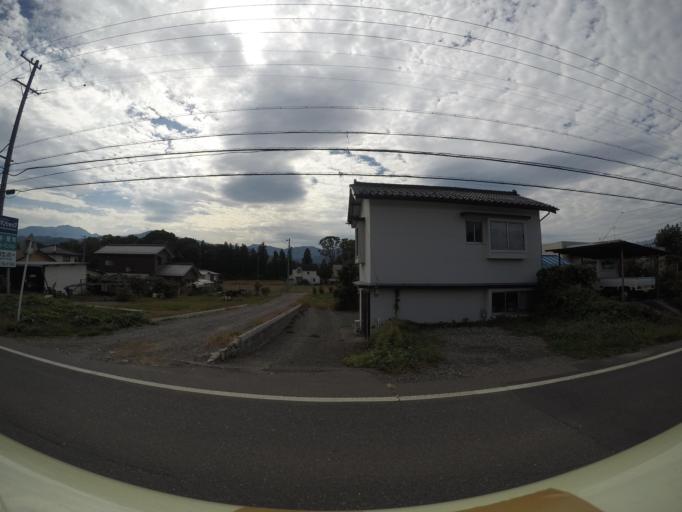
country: JP
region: Nagano
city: Ina
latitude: 35.8405
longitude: 138.0232
